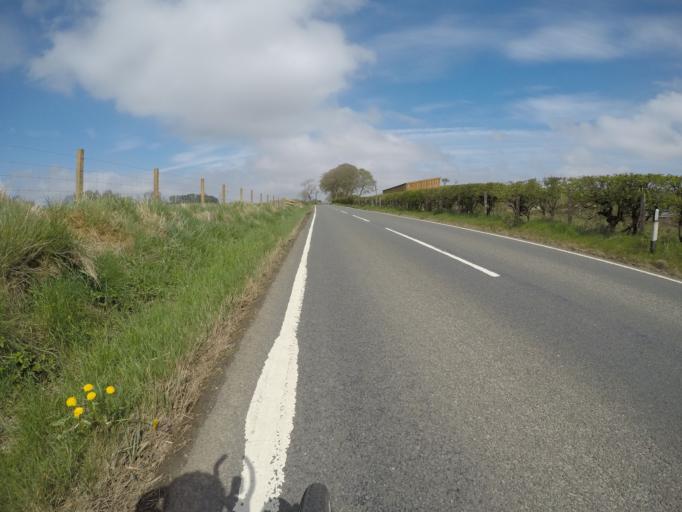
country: GB
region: Scotland
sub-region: East Ayrshire
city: Stewarton
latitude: 55.7065
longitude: -4.4621
